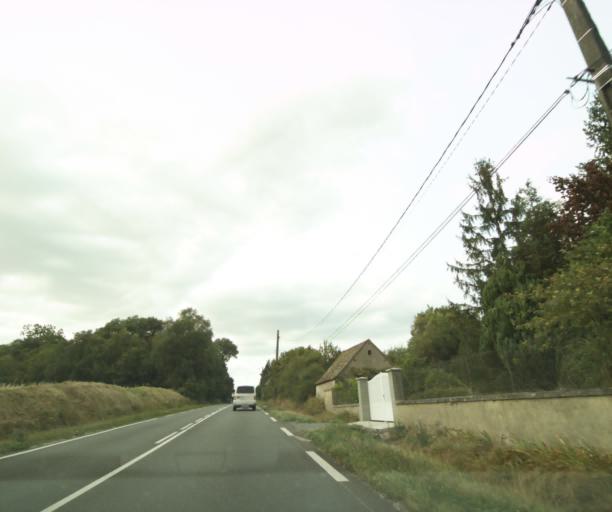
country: FR
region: Centre
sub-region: Departement d'Indre-et-Loire
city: Loches
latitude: 47.1568
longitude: 0.9946
